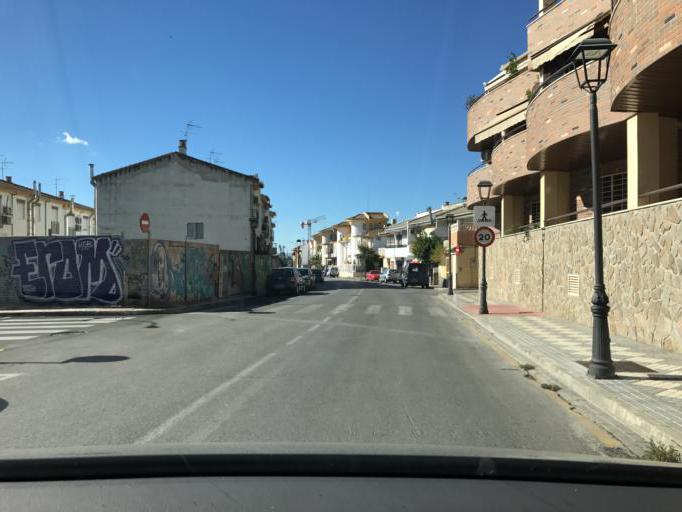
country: ES
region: Andalusia
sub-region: Provincia de Granada
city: Maracena
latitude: 37.2066
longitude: -3.6400
